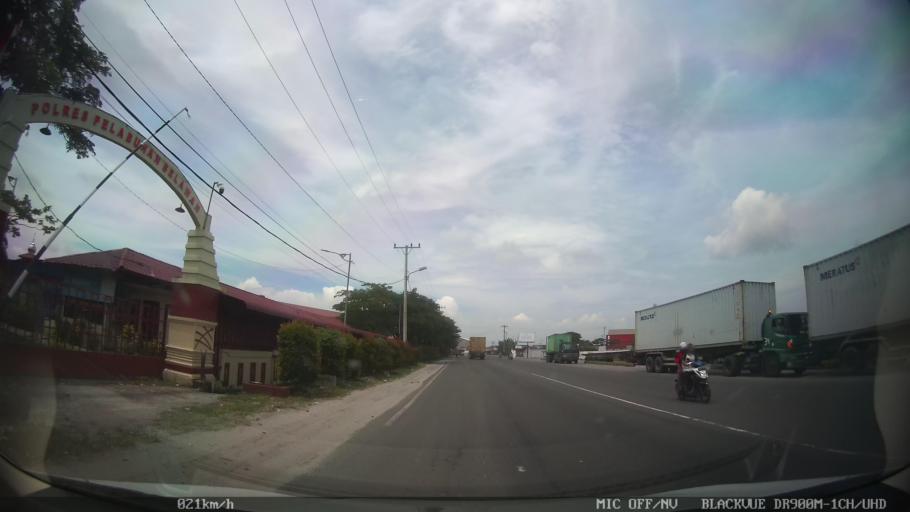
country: ID
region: North Sumatra
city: Belawan
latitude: 3.7781
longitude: 98.7045
